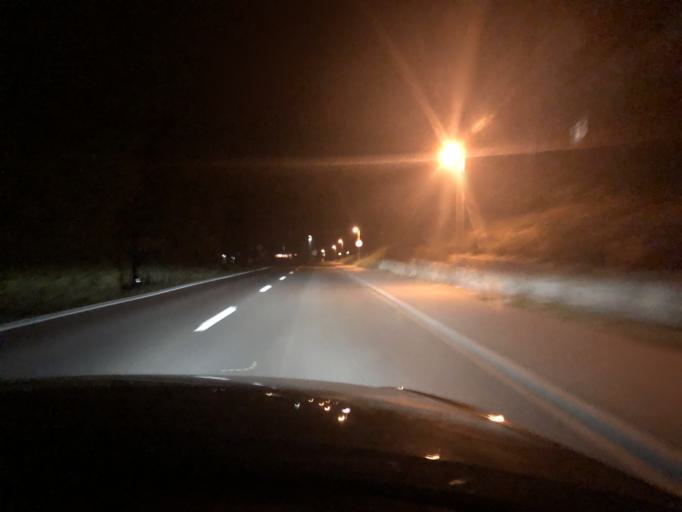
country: CH
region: Aargau
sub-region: Bezirk Baden
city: Unterehrendingen
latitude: 47.5151
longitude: 8.3662
